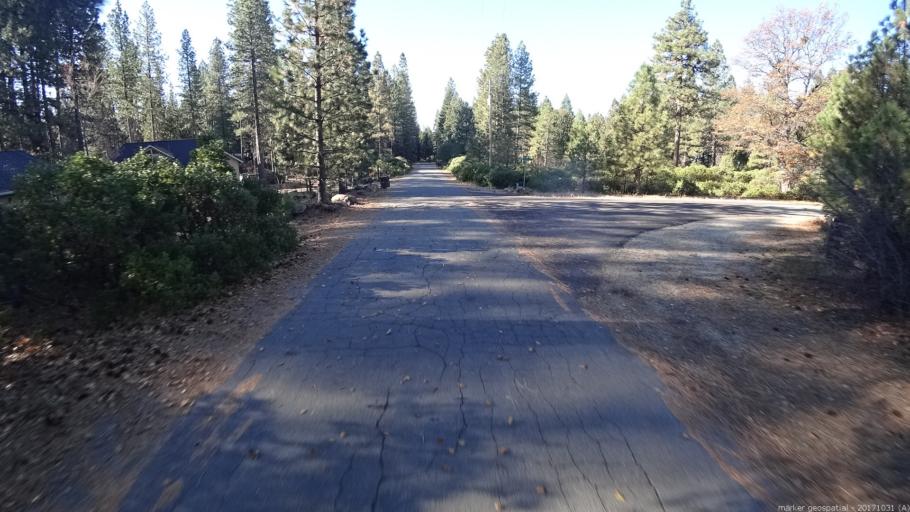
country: US
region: California
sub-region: Shasta County
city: Shingletown
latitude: 40.5122
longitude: -121.8227
